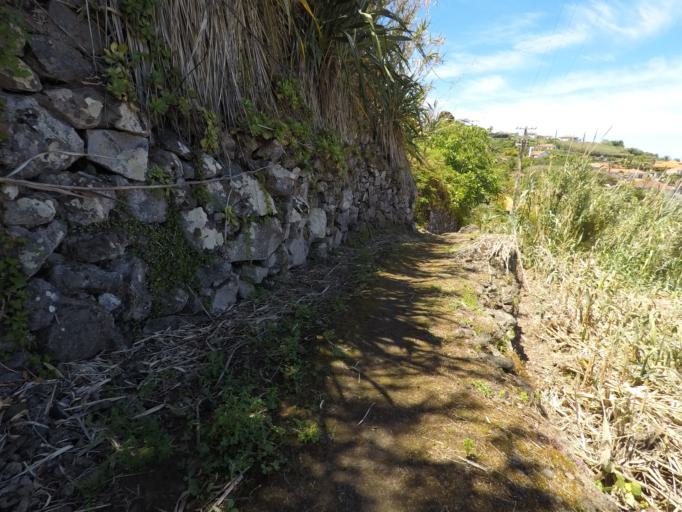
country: PT
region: Madeira
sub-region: Sao Vicente
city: Sao Vicente
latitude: 32.8261
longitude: -16.9845
